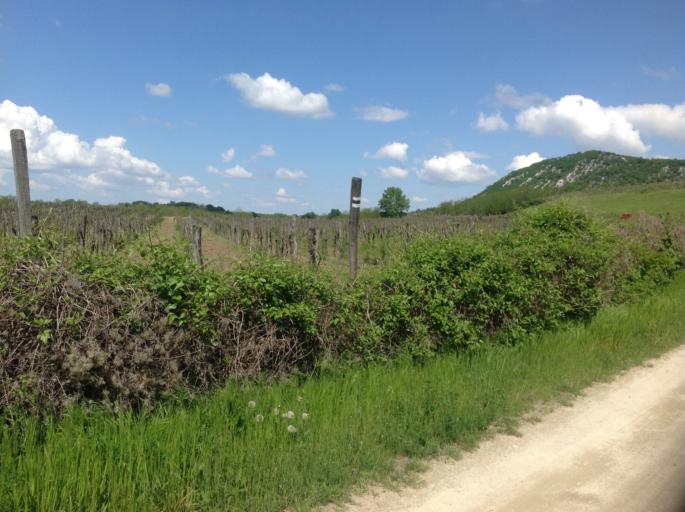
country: HU
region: Komarom-Esztergom
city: Kesztolc
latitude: 47.7152
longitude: 18.7988
